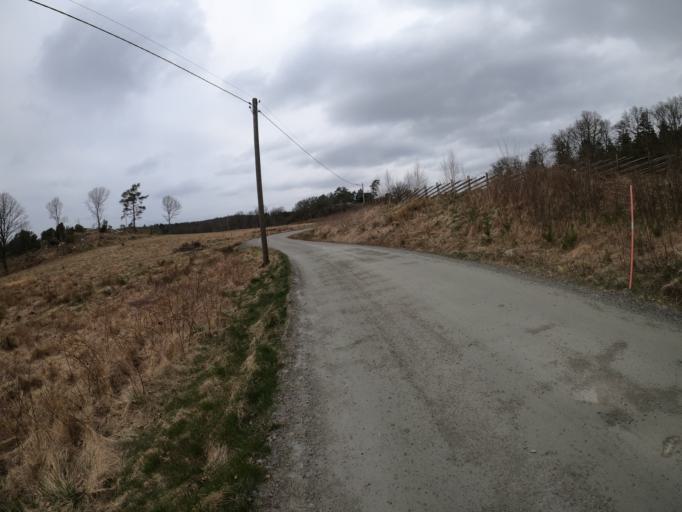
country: SE
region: Vaestra Goetaland
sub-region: Harryda Kommun
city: Molnlycke
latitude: 57.6279
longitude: 12.1081
